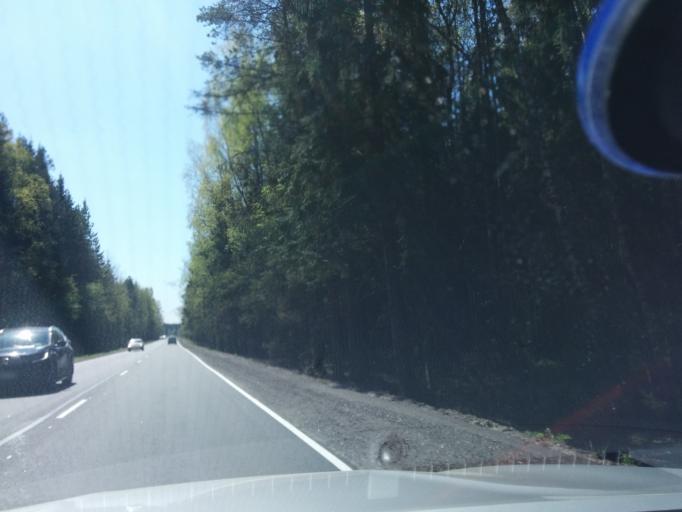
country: RU
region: Leningrad
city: Verkhniye Osel'ki
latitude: 60.2100
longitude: 30.4265
